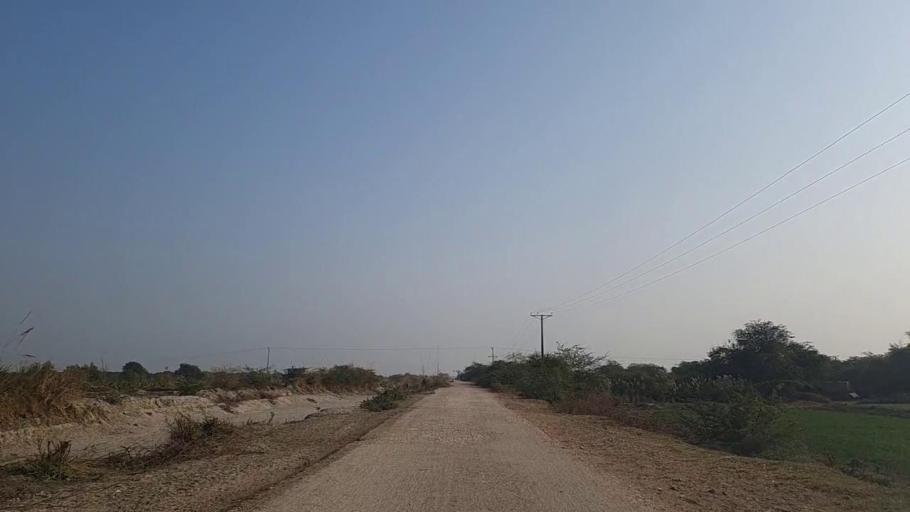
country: PK
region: Sindh
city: Jam Sahib
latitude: 26.2376
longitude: 68.5911
